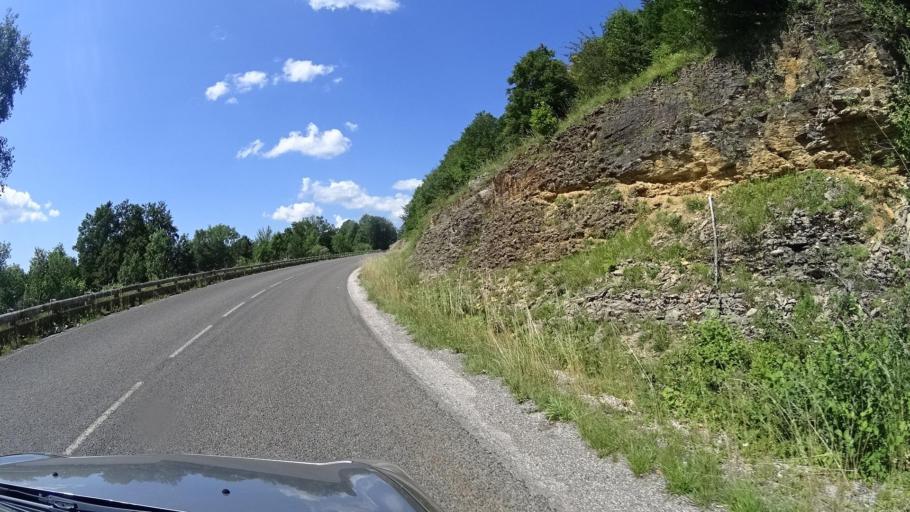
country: FR
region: Franche-Comte
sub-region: Departement du Jura
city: Longchaumois
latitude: 46.5054
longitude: 5.9501
